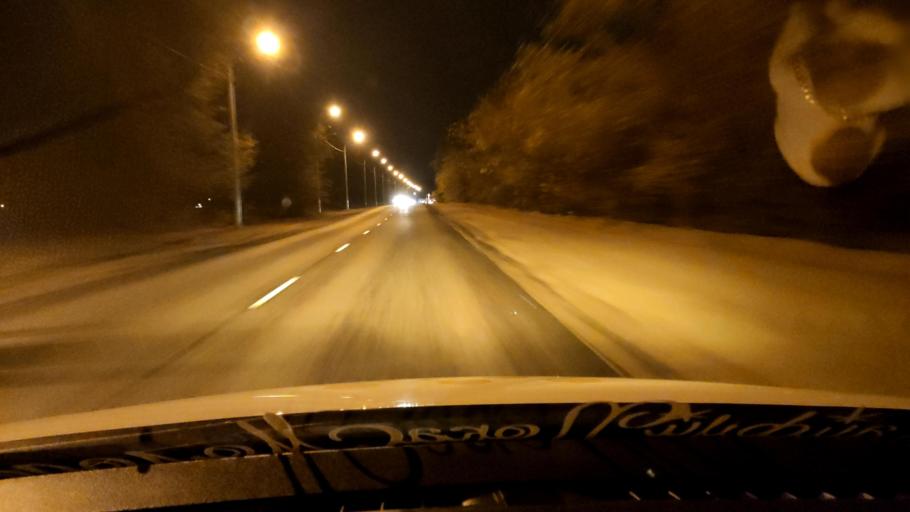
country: RU
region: Voronezj
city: Pridonskoy
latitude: 51.6919
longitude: 39.0837
